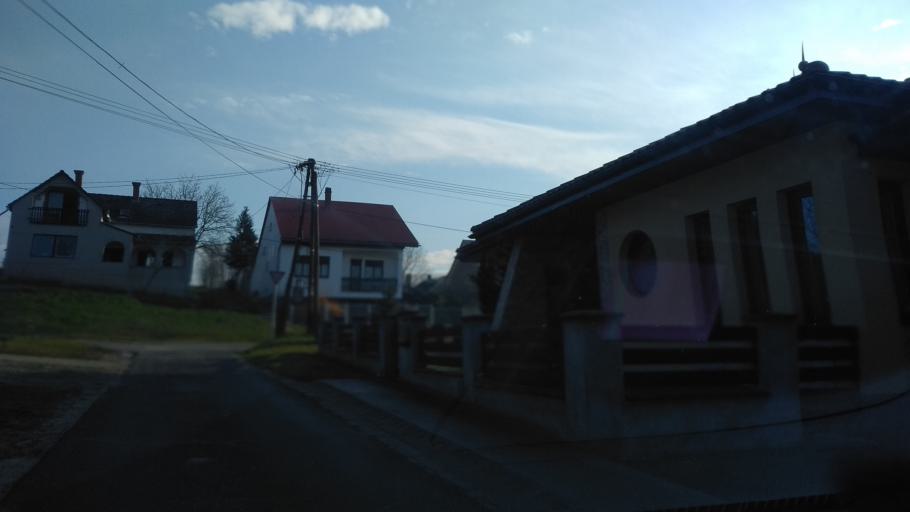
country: HU
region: Somogy
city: Barcs
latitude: 45.9657
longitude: 17.4771
